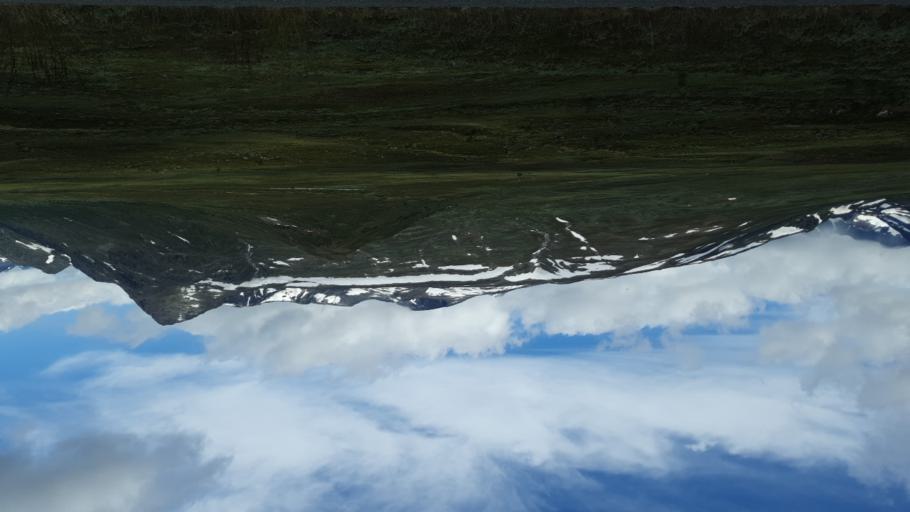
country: NO
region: Oppland
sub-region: Vang
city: Vang
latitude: 61.4527
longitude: 8.8061
